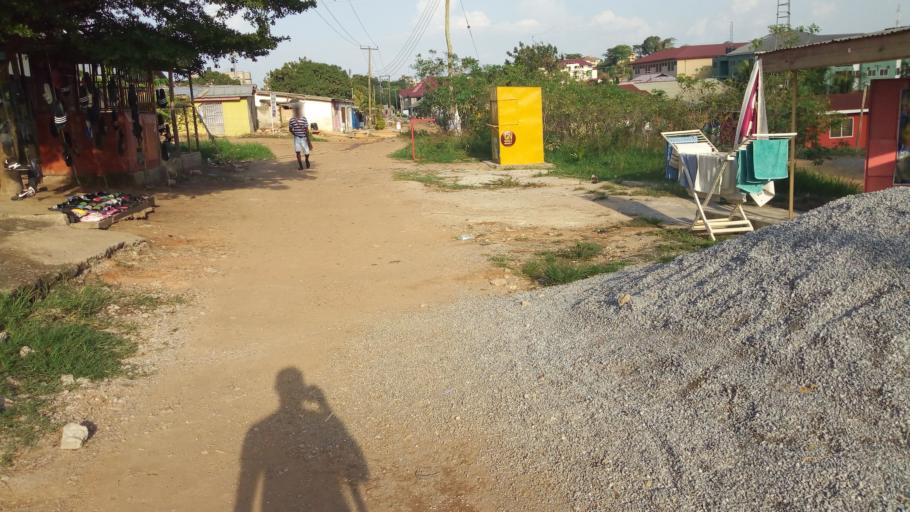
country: GH
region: Ashanti
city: Mamponteng
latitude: 6.6737
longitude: -1.5626
